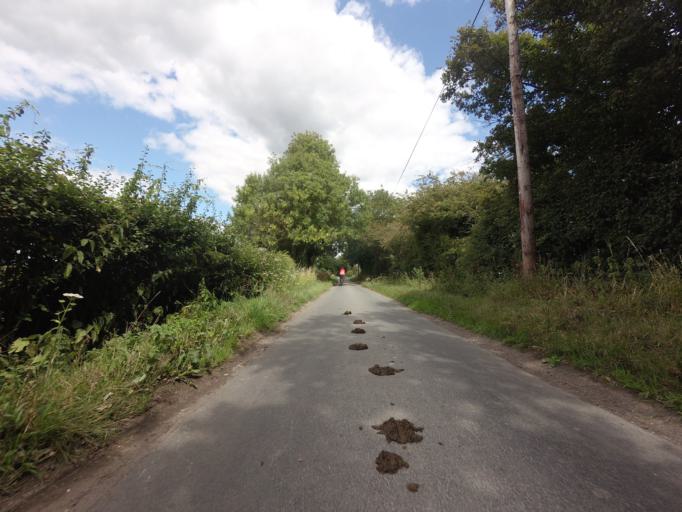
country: GB
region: England
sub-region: East Sussex
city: Pevensey
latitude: 50.8357
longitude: 0.2998
